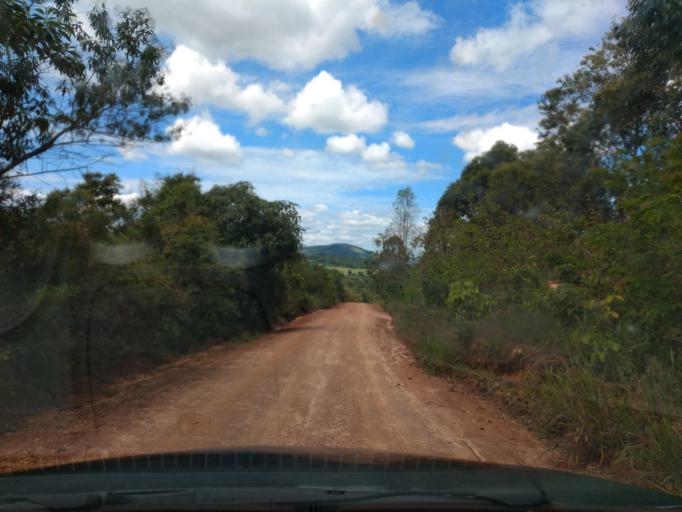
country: BR
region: Minas Gerais
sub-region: Lavras
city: Lavras
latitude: -21.5110
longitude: -44.9274
